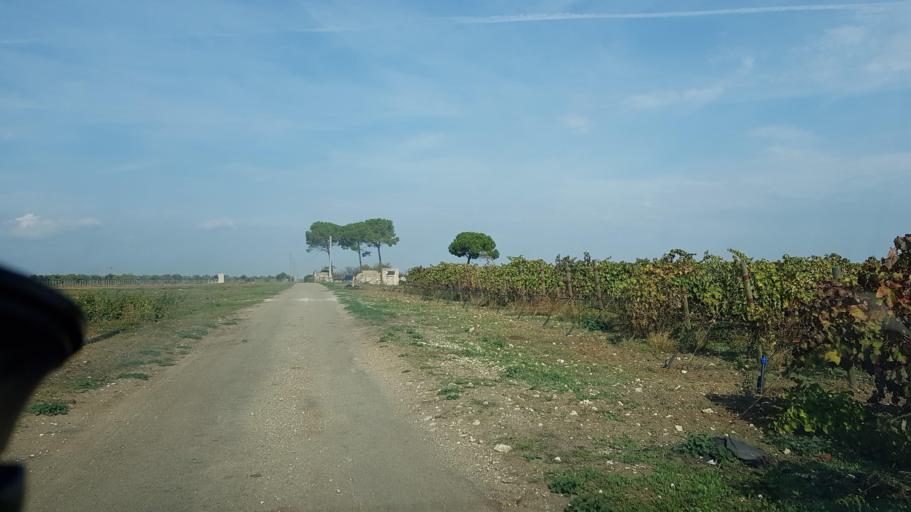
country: IT
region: Apulia
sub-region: Provincia di Brindisi
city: San Pancrazio Salentino
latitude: 40.4257
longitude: 17.8599
